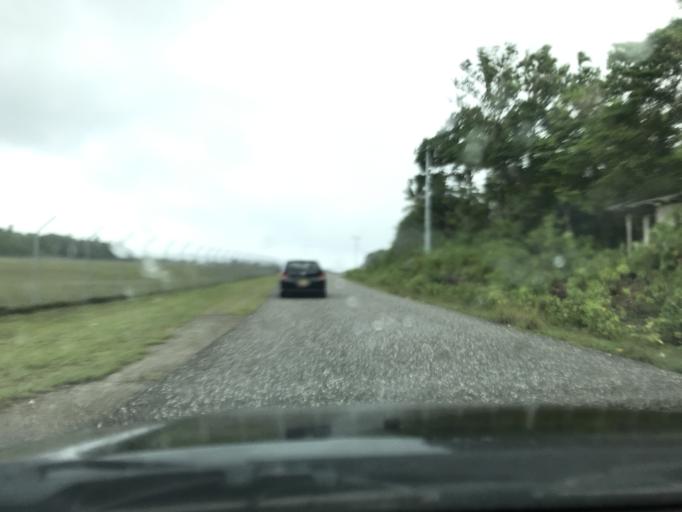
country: SB
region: Western Province
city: Gizo
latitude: -8.3264
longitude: 157.2613
